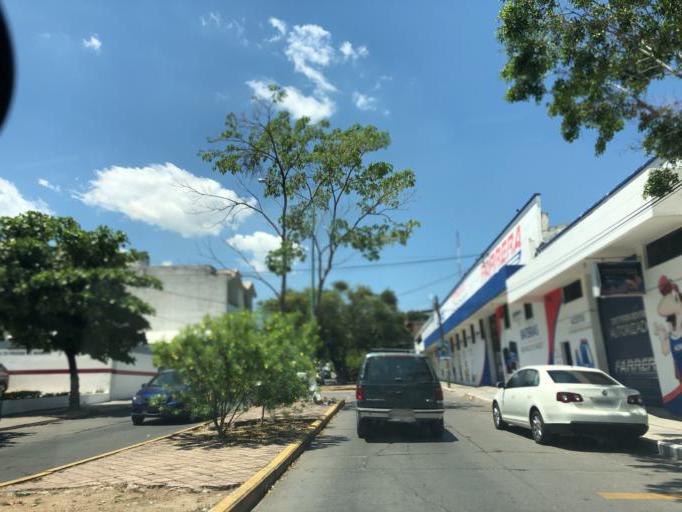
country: MX
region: Chiapas
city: Tuxtla Gutierrez
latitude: 16.7549
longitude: -93.1258
